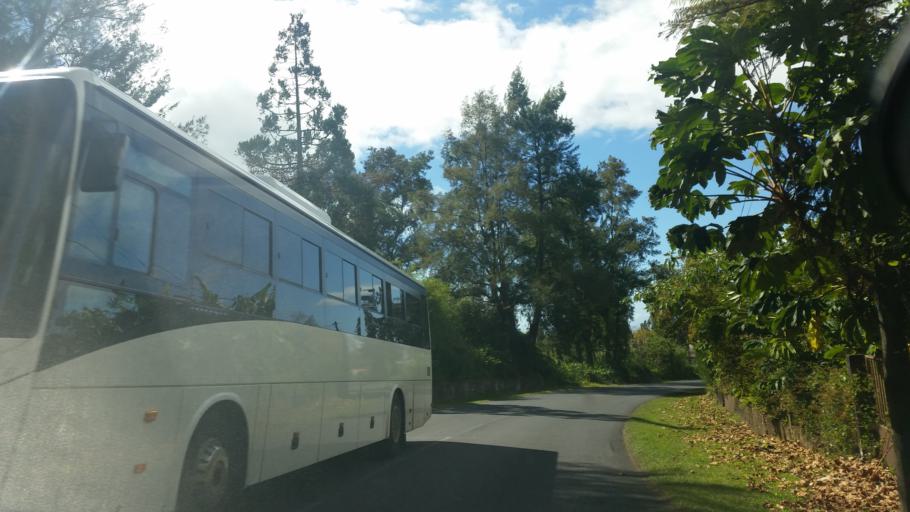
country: RE
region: Reunion
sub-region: Reunion
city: Saint-Benoit
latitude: -21.1317
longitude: 55.6322
